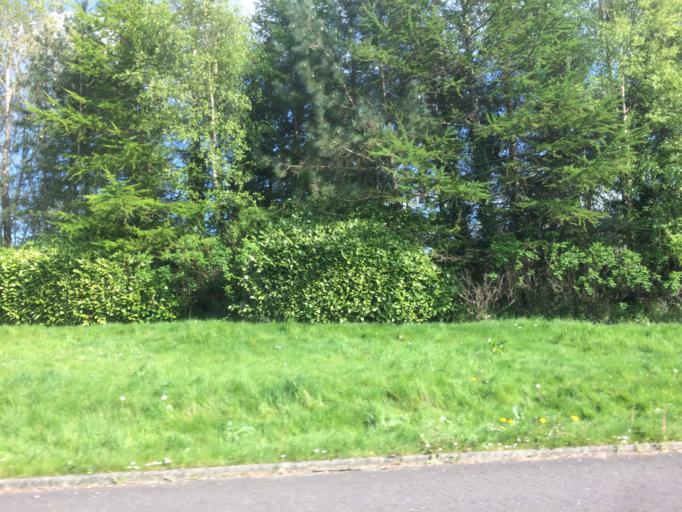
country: GB
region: Scotland
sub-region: East Renfrewshire
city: Newton Mearns
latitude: 55.8028
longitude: -4.3417
